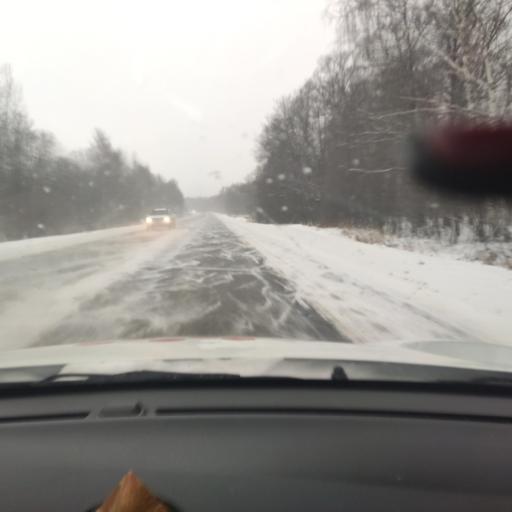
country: RU
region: Tatarstan
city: Verkhniy Uslon
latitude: 55.6929
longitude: 48.8782
